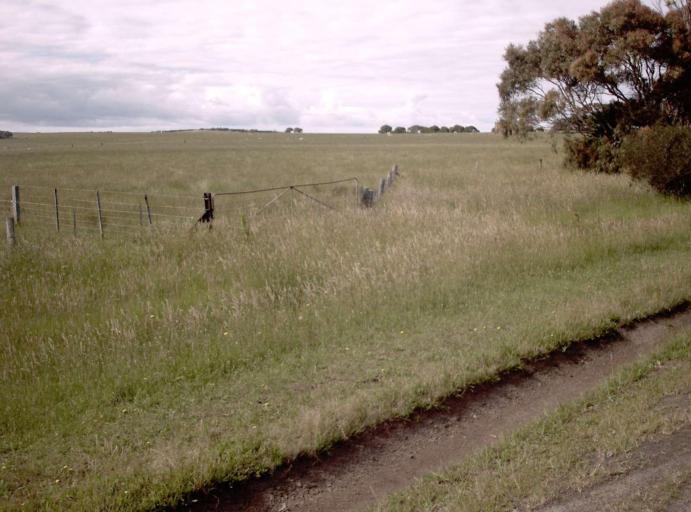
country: AU
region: Victoria
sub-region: Bass Coast
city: Phillip Island
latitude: -38.4778
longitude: 145.1812
